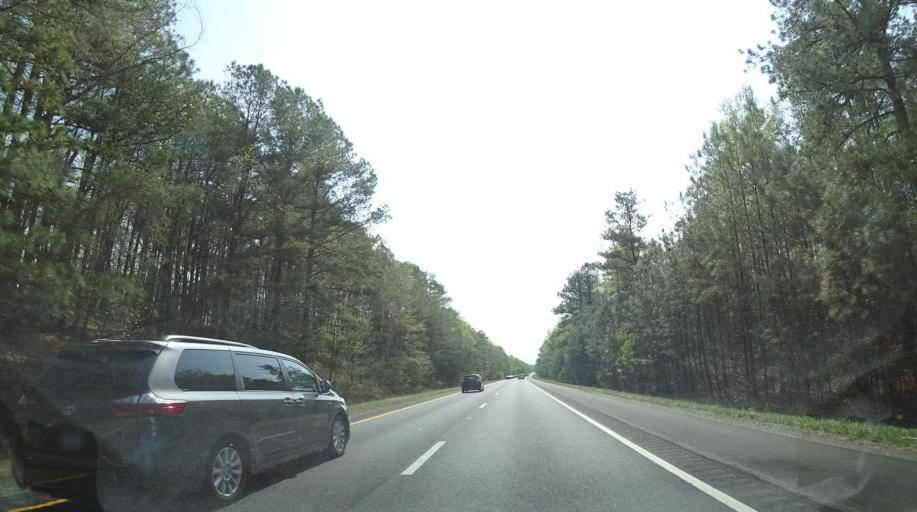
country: US
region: Virginia
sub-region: New Kent County
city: New Kent
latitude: 37.4737
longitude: -76.9085
